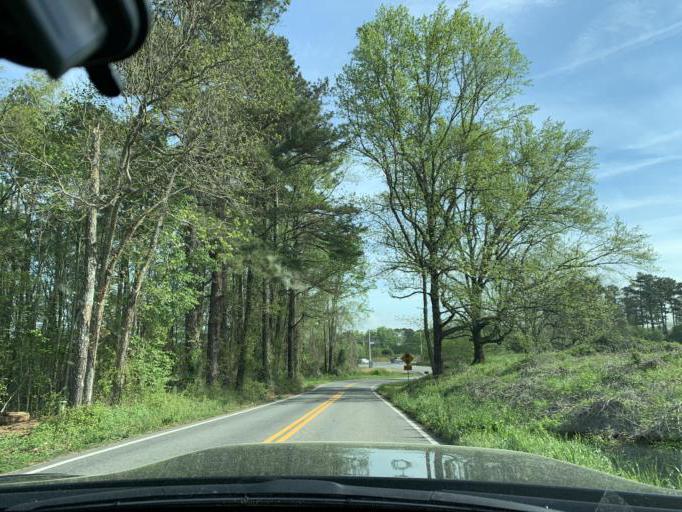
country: US
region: Georgia
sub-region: Forsyth County
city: Cumming
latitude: 34.2526
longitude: -84.1443
